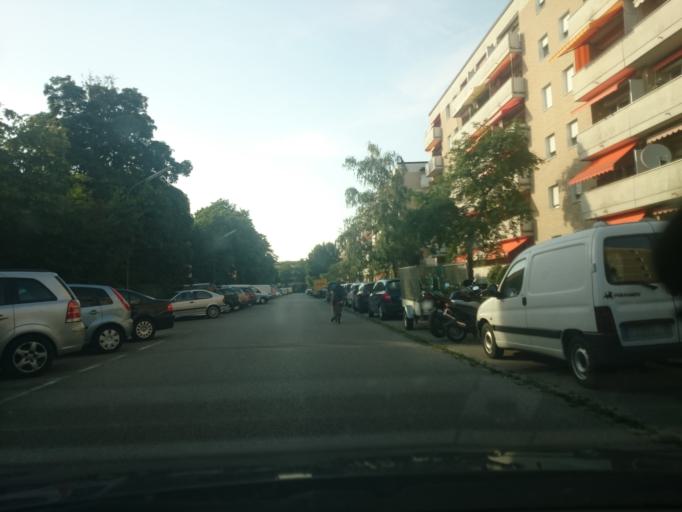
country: DE
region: Bavaria
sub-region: Upper Bavaria
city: Germering
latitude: 48.1318
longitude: 11.3611
